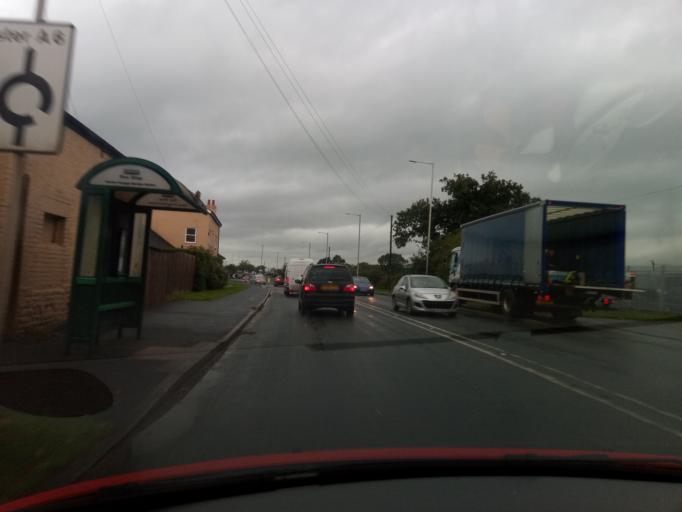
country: GB
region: England
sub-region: Lancashire
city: Catterall
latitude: 53.8607
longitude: -2.7439
